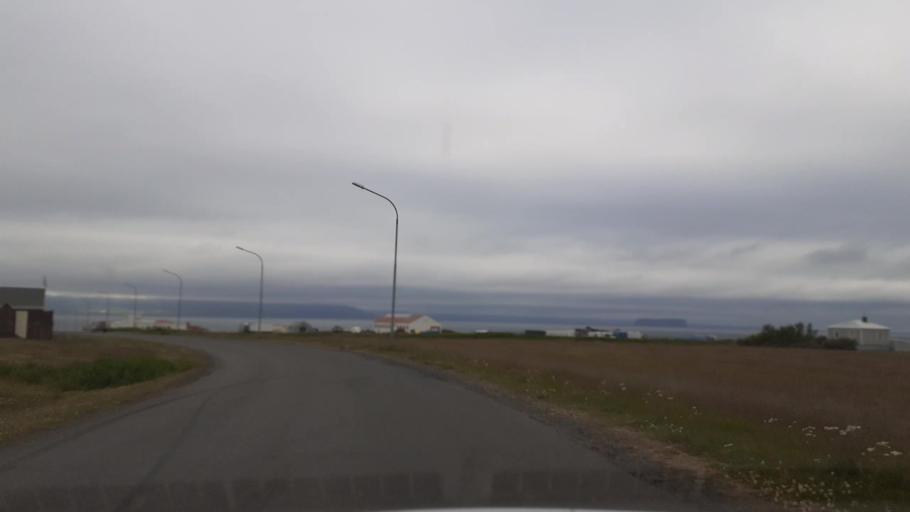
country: IS
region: Northwest
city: Saudarkrokur
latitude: 65.9010
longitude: -19.4181
